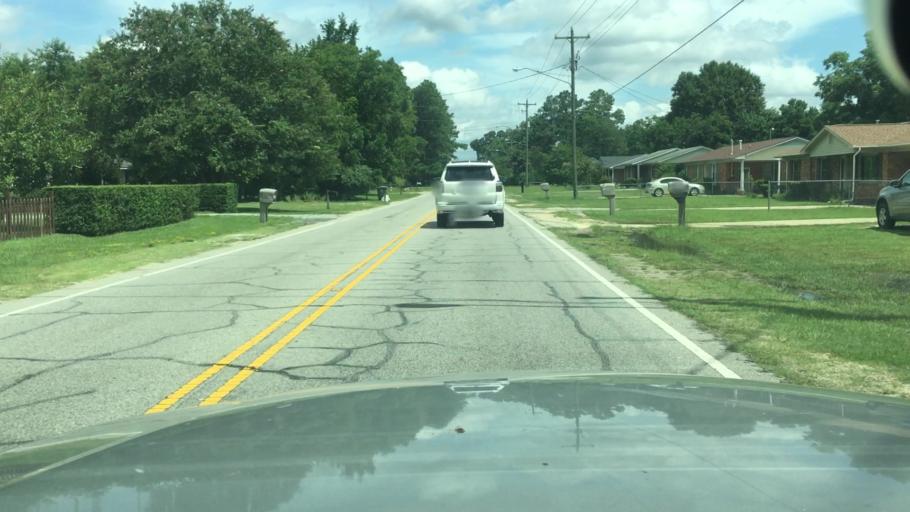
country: US
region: North Carolina
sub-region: Hoke County
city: Rockfish
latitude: 35.0340
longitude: -78.9974
